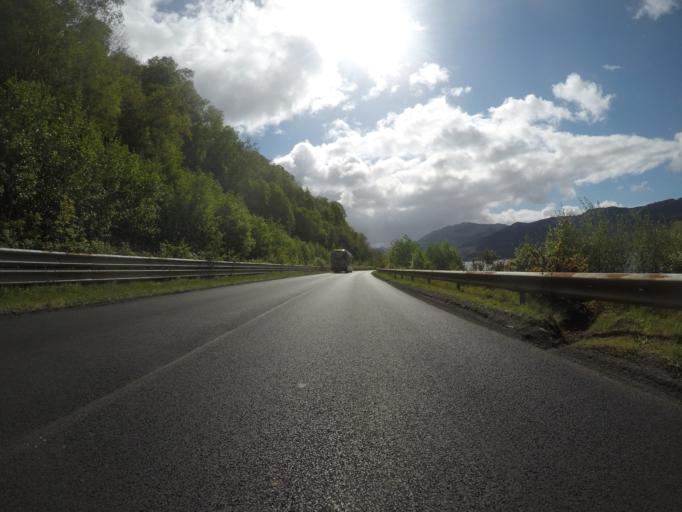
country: GB
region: Scotland
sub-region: Highland
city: Fort William
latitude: 57.2536
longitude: -5.4762
